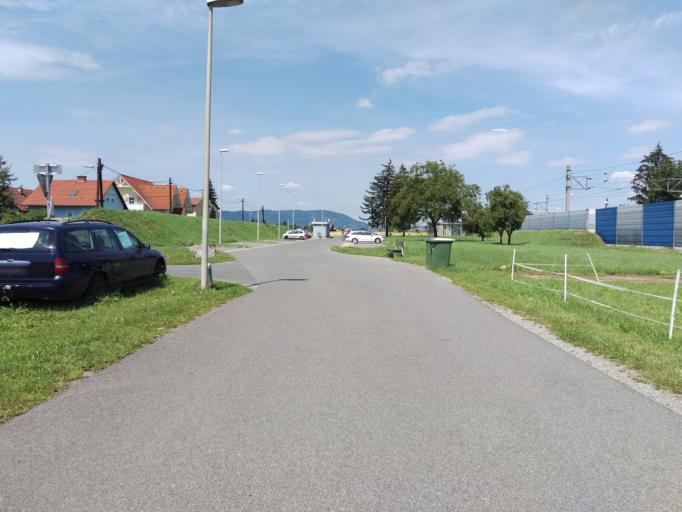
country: AT
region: Styria
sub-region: Politischer Bezirk Graz-Umgebung
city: Feldkirchen bei Graz
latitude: 47.0113
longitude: 15.4409
